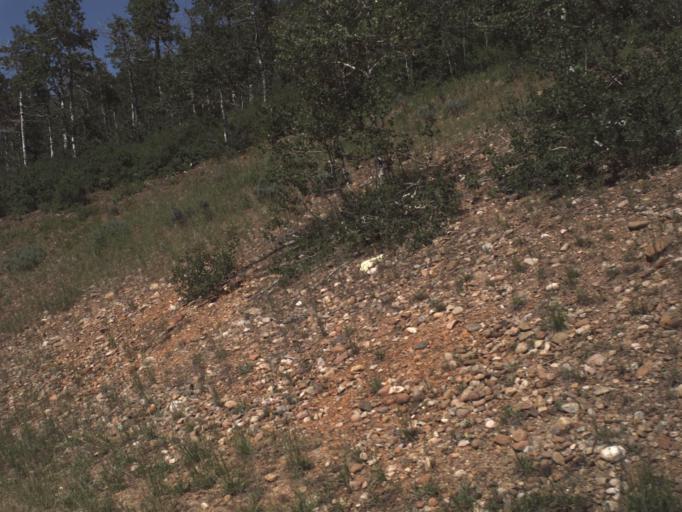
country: US
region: Utah
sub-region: Weber County
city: Wolf Creek
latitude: 41.4024
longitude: -111.5461
